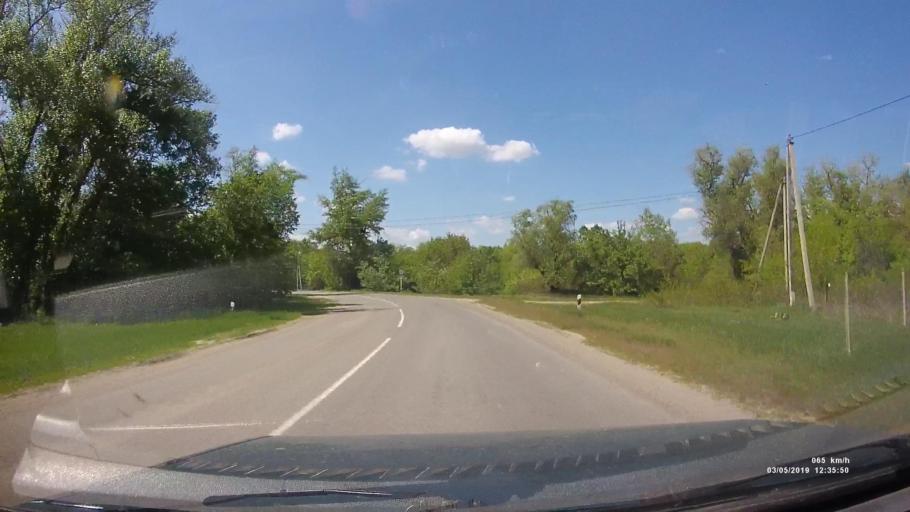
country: RU
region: Rostov
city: Semikarakorsk
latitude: 47.5291
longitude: 40.7569
